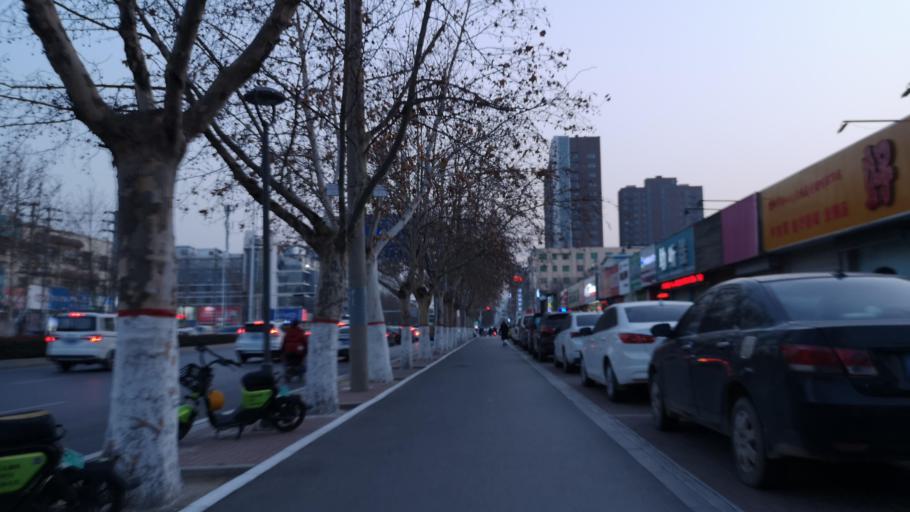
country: CN
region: Henan Sheng
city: Zhongyuanlu
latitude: 35.7703
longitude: 115.0692
